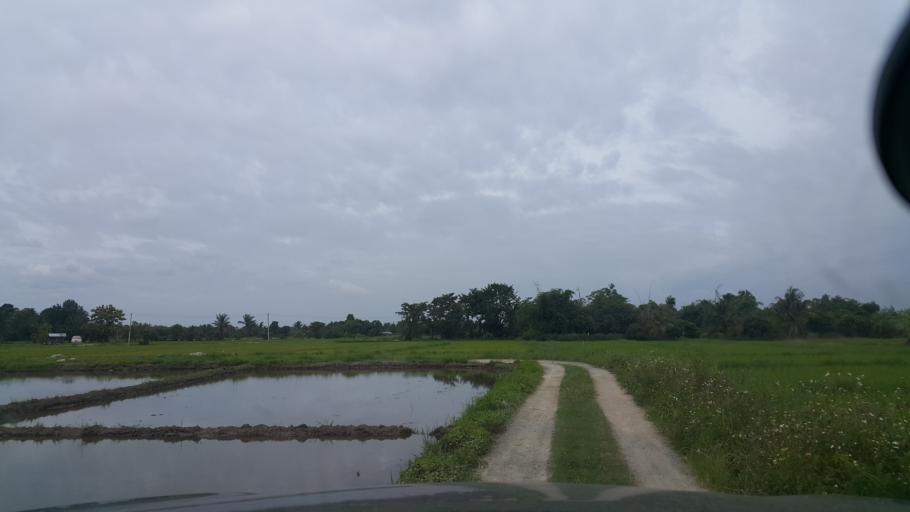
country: TH
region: Chiang Mai
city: San Kamphaeng
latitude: 18.7585
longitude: 99.1656
